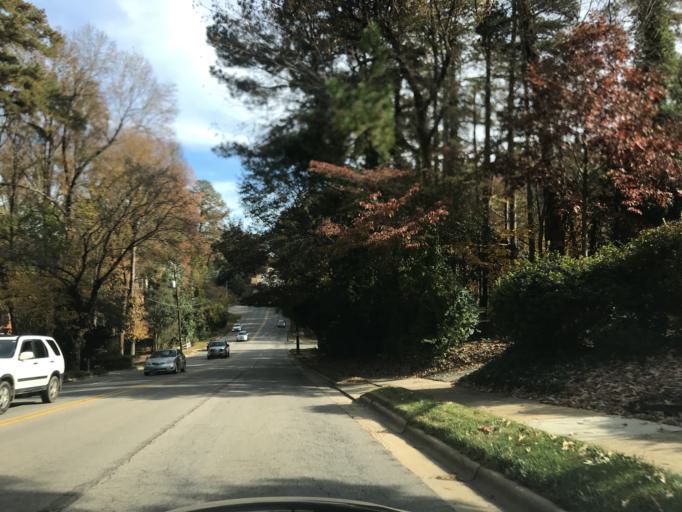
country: US
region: North Carolina
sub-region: Wake County
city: West Raleigh
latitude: 35.8004
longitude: -78.6678
